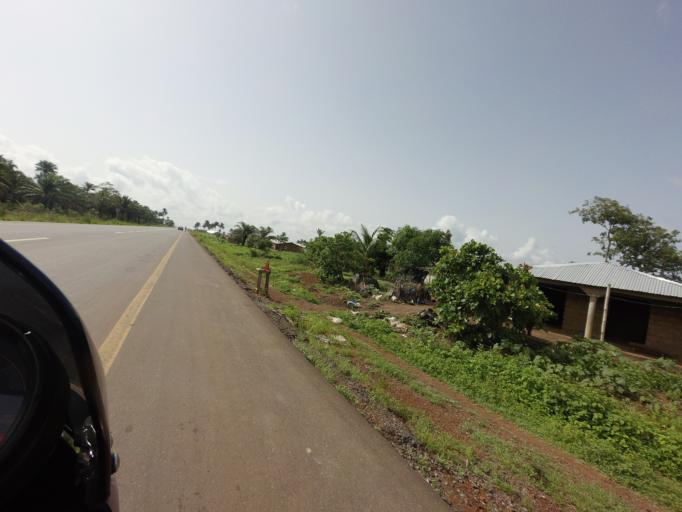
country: SL
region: Northern Province
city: Kambia
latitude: 9.0496
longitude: -12.9131
